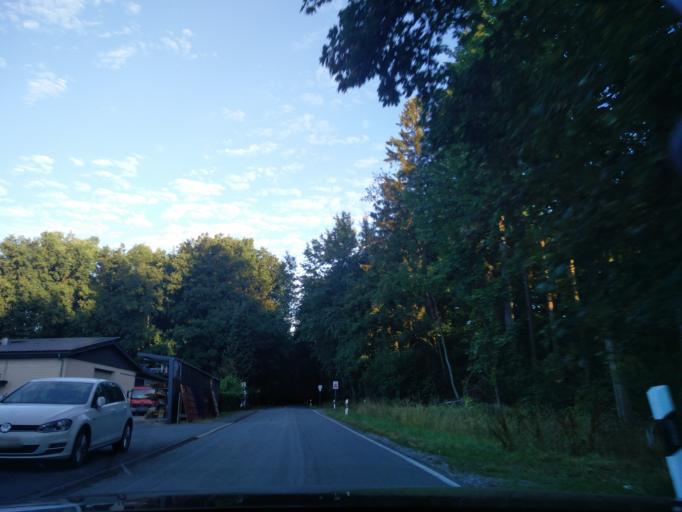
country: DE
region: North Rhine-Westphalia
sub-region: Regierungsbezirk Detmold
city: Bad Driburg
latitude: 51.6775
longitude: 8.9746
